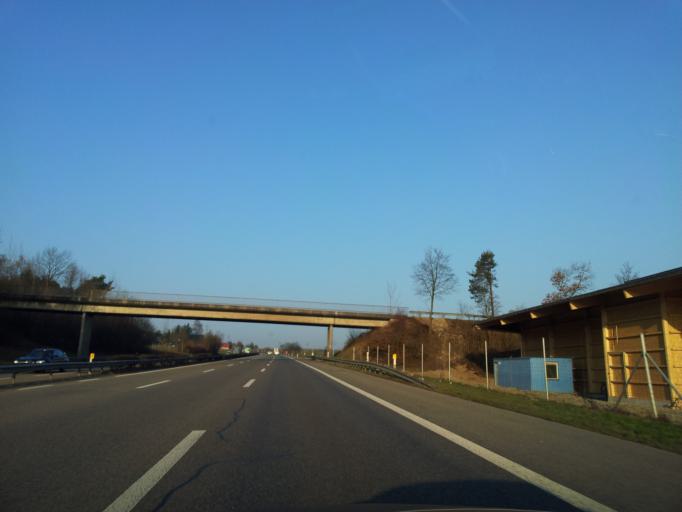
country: CH
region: Aargau
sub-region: Bezirk Rheinfelden
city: Mumpf
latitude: 47.5512
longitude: 7.8977
